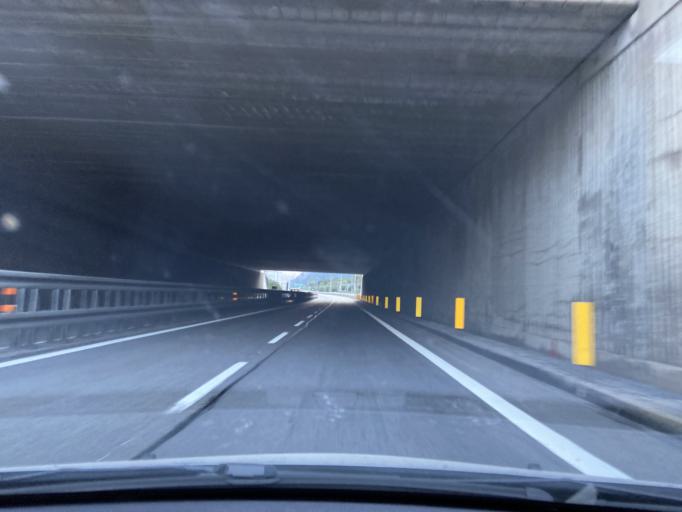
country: IT
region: Piedmont
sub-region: Provincia di Torino
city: Salbertrand
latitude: 45.0688
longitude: 6.8828
